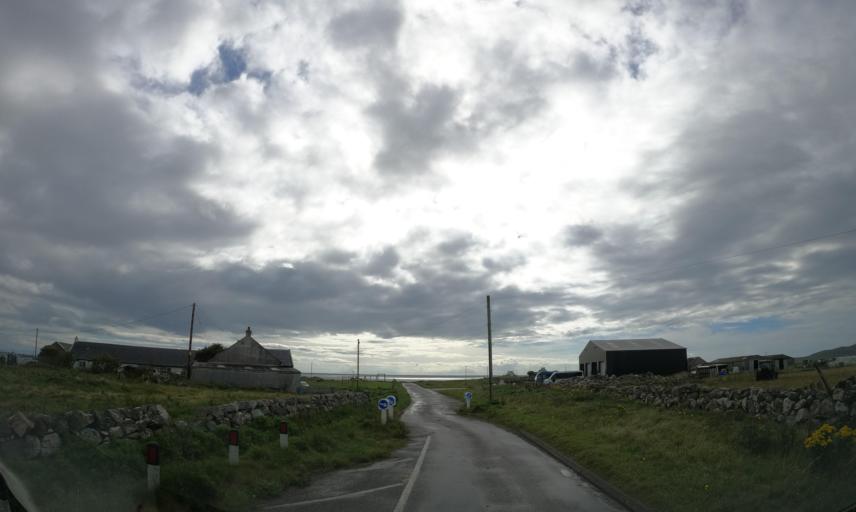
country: GB
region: Scotland
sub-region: Eilean Siar
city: Barra
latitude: 56.4904
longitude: -6.8815
